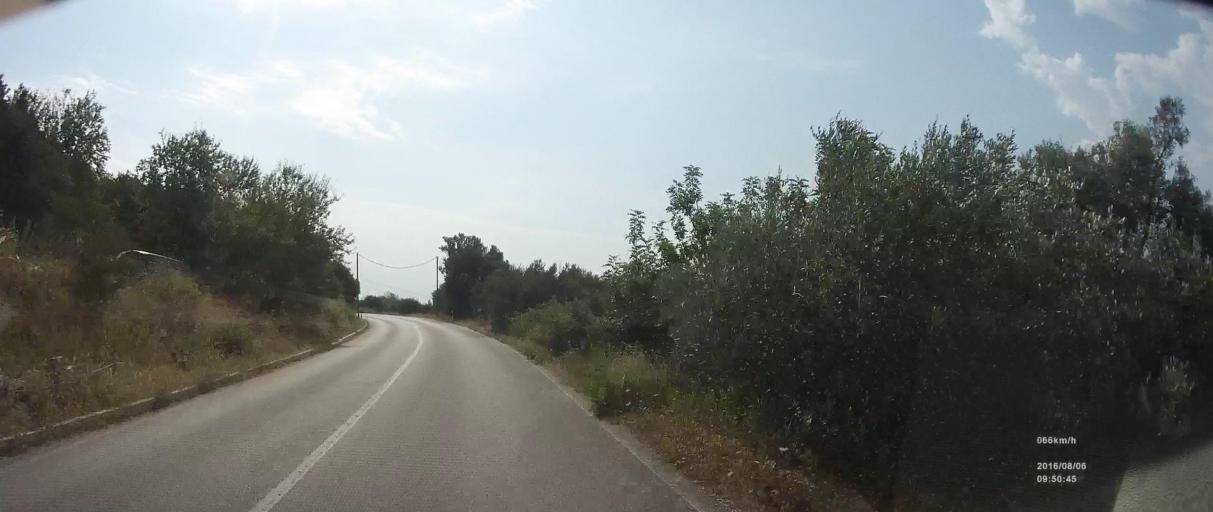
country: HR
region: Dubrovacko-Neretvanska
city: Blato
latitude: 42.7326
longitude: 17.5564
